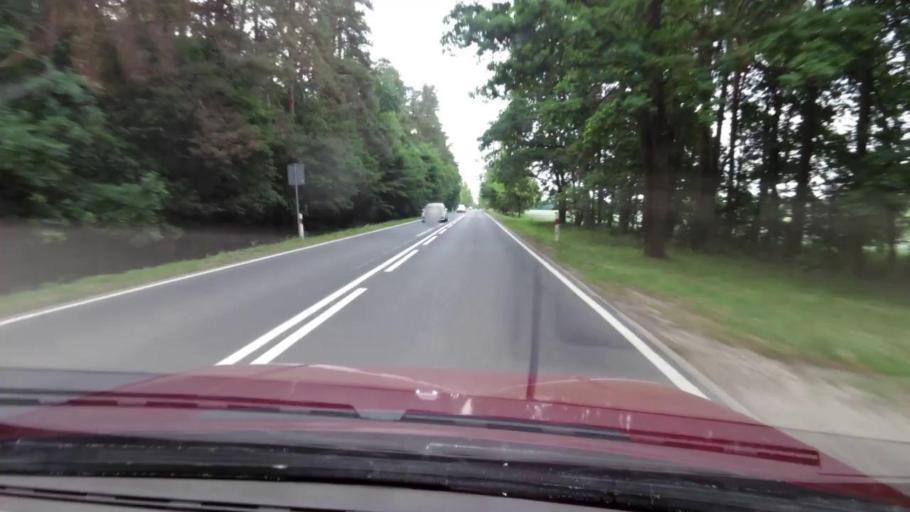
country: PL
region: Pomeranian Voivodeship
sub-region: Powiat bytowski
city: Trzebielino
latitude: 54.2564
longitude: 17.1039
